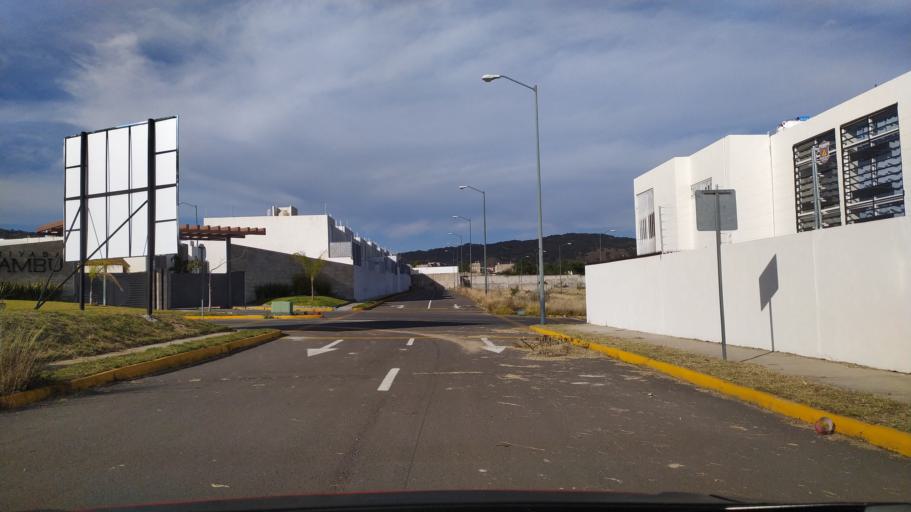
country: MX
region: Jalisco
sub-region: Tlajomulco de Zuniga
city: Palomar
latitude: 20.6325
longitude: -103.4827
